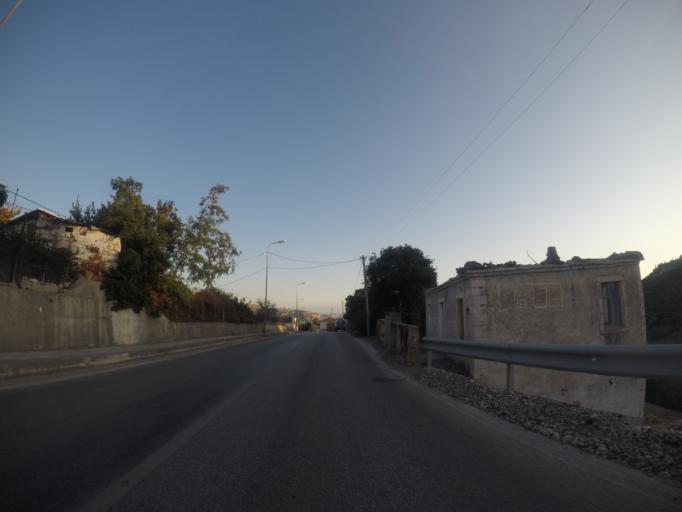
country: AL
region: Vlore
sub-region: Rrethi i Vlores
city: Himare
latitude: 40.1121
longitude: 19.7392
